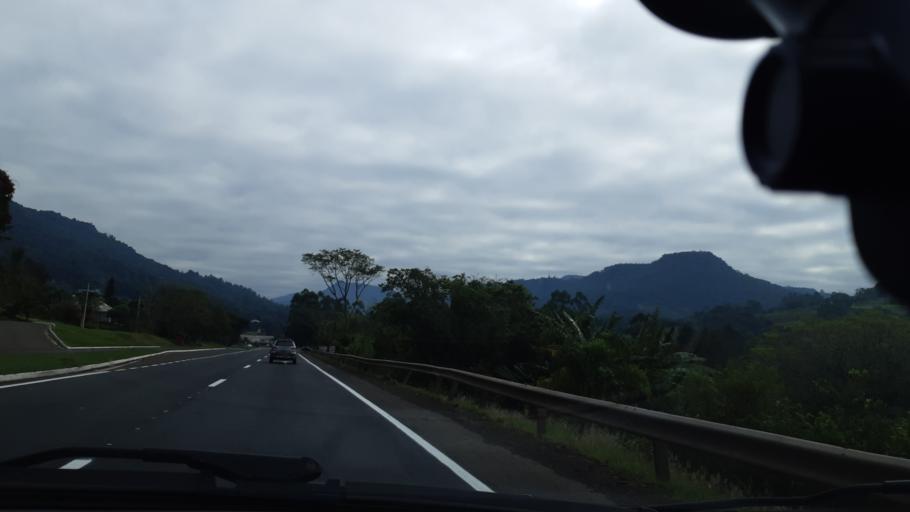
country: BR
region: Rio Grande do Sul
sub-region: Farroupilha
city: Farroupilha
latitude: -29.4044
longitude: -51.3539
